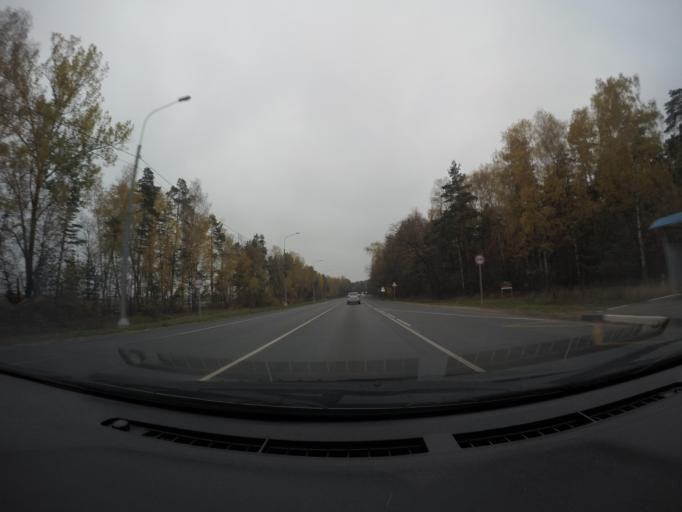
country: RU
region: Moskovskaya
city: Malyshevo
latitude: 55.4474
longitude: 38.3223
